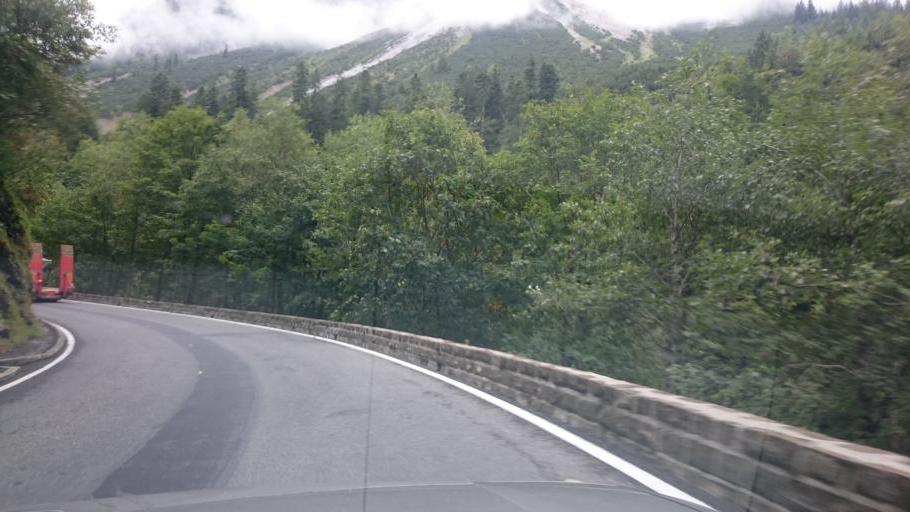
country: AT
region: Vorarlberg
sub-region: Politischer Bezirk Bregenz
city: Schoppernau
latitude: 47.2884
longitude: 10.0449
